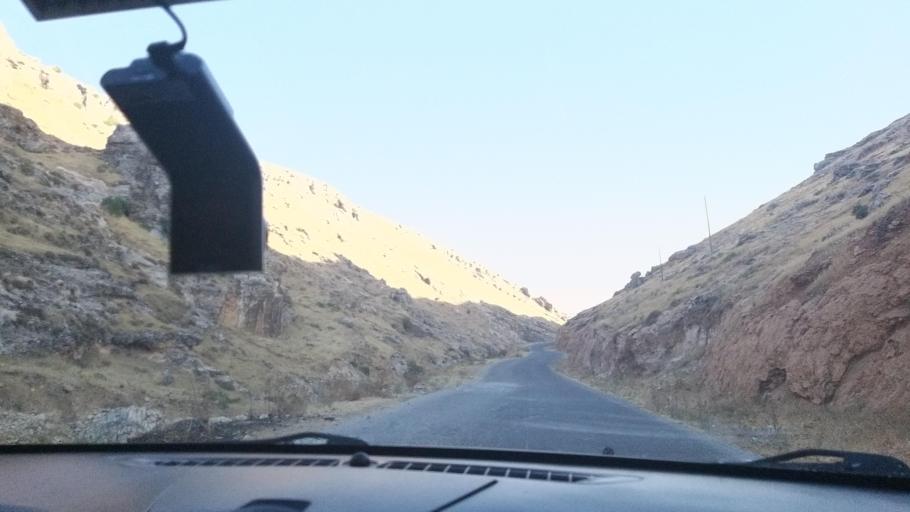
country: TR
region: Diyarbakir
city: Silvan
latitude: 38.1627
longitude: 41.0019
